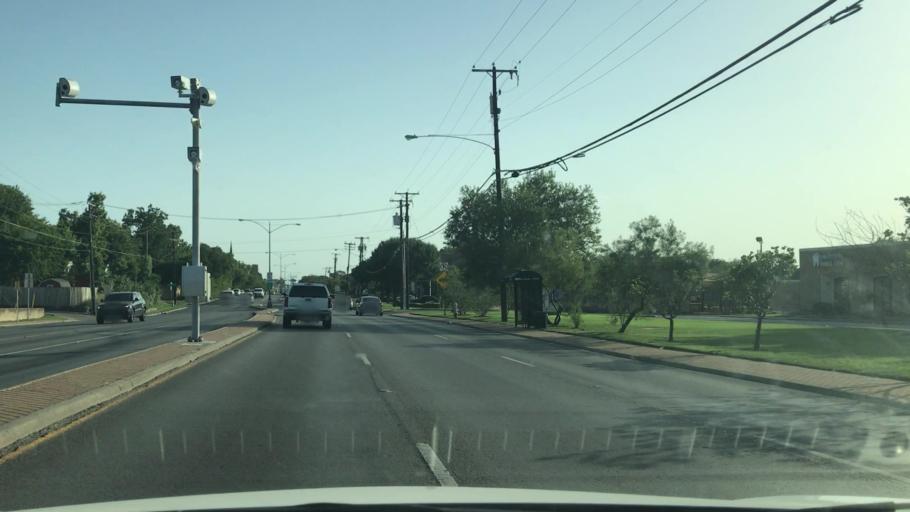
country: US
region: Texas
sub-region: Dallas County
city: Highland Park
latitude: 32.8336
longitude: -96.7026
